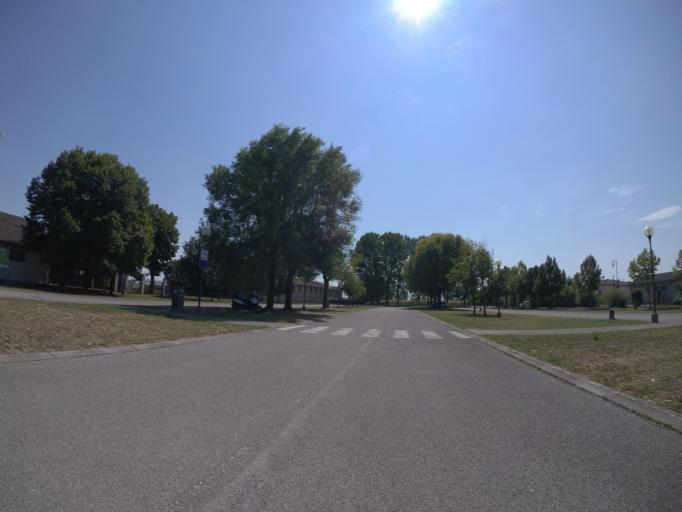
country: IT
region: Friuli Venezia Giulia
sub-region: Provincia di Udine
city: Codroipo
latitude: 45.9472
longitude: 13.0086
